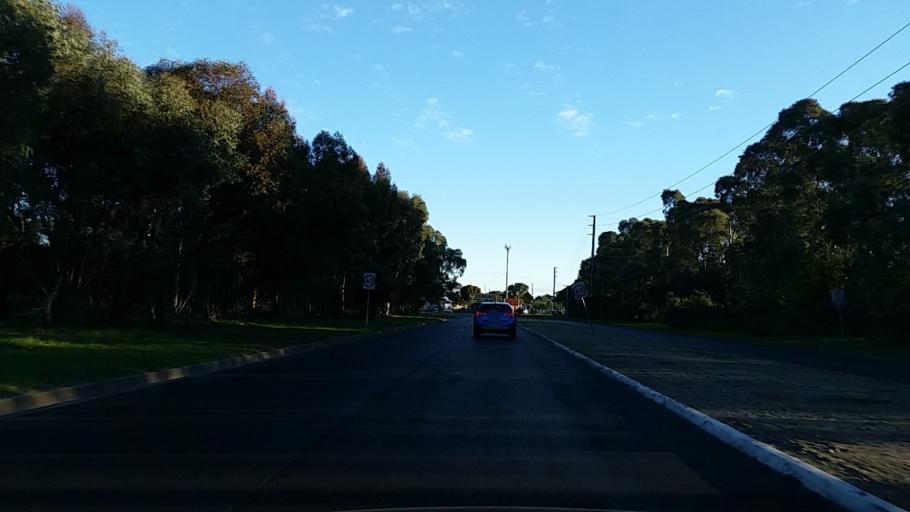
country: AU
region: South Australia
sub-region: Salisbury
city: Salisbury
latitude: -34.7484
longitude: 138.6459
